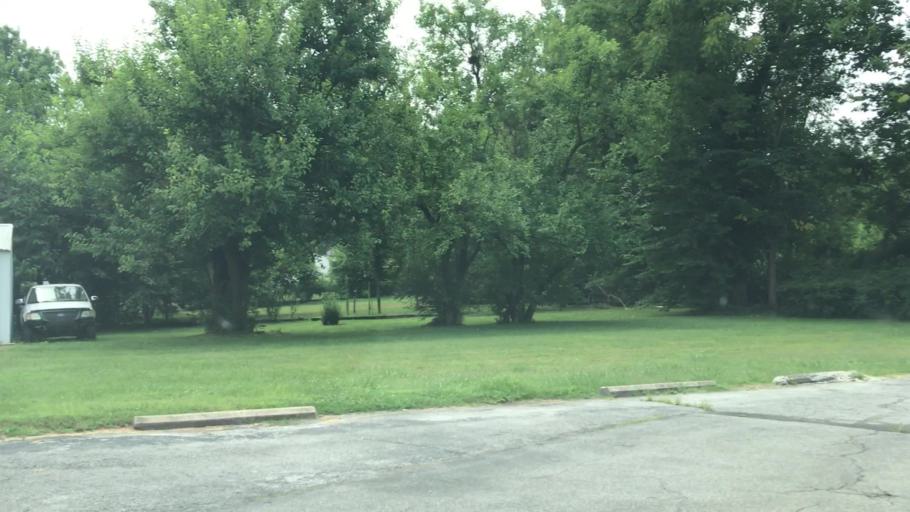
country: US
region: Kentucky
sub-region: Warren County
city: Bowling Green
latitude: 36.9746
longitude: -86.4394
